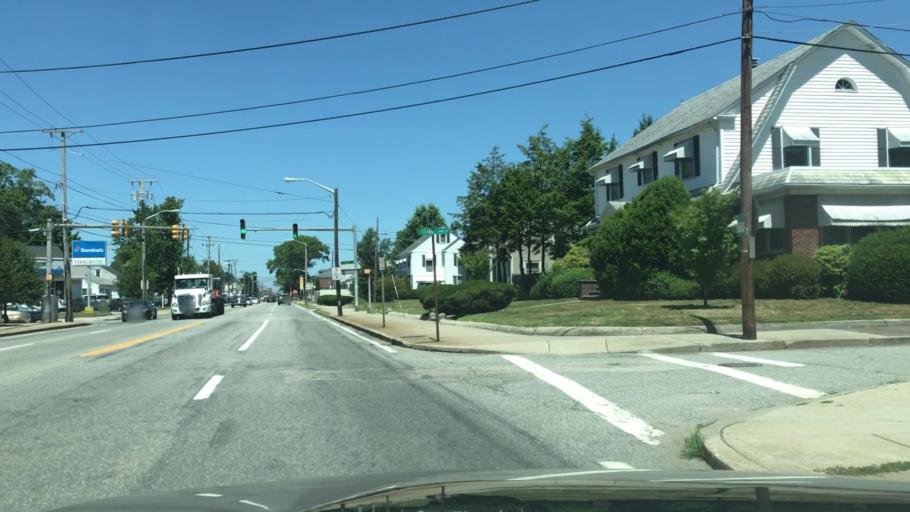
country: US
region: Rhode Island
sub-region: Providence County
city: Pawtucket
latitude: 41.8696
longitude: -71.3544
